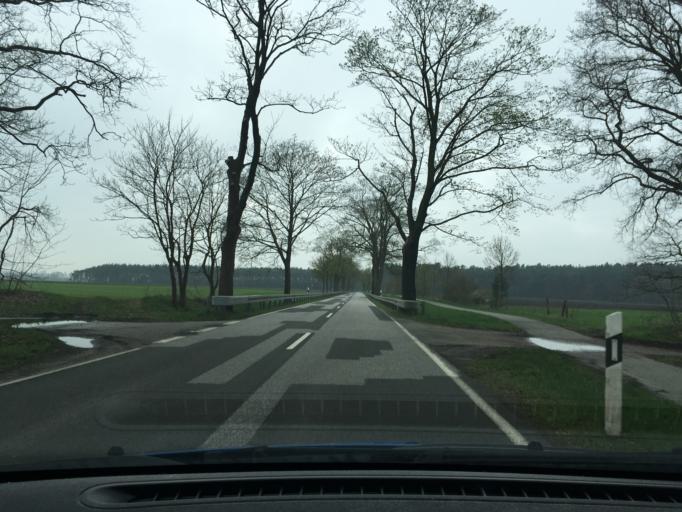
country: DE
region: Mecklenburg-Vorpommern
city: Boizenburg
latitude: 53.3619
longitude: 10.7791
